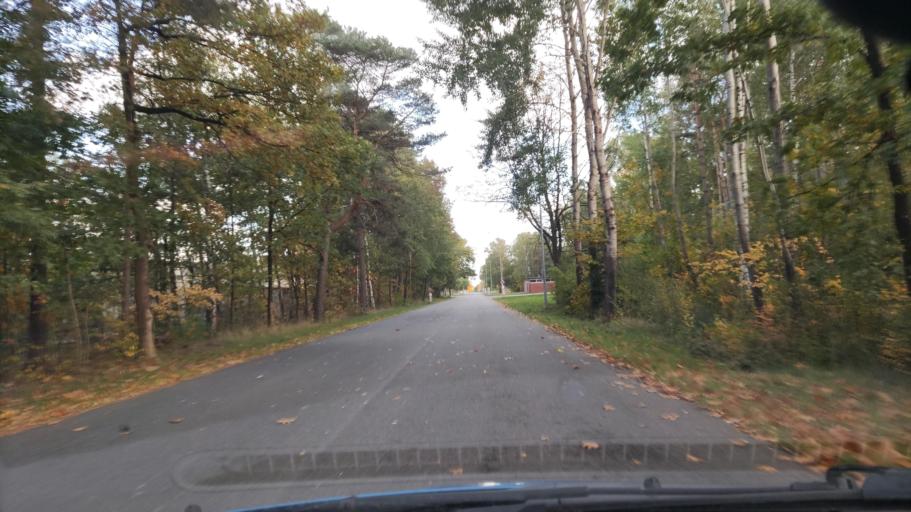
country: DE
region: Lower Saxony
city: Munster
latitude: 52.9853
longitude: 10.0606
